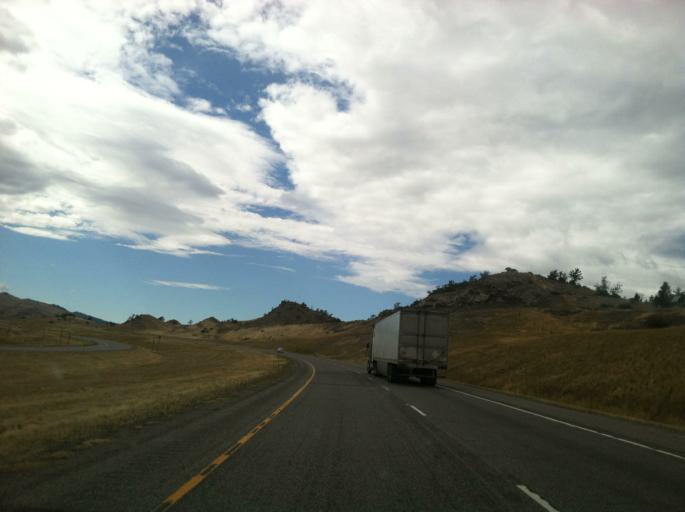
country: US
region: Montana
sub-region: Park County
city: Livingston
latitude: 45.6621
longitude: -110.6425
